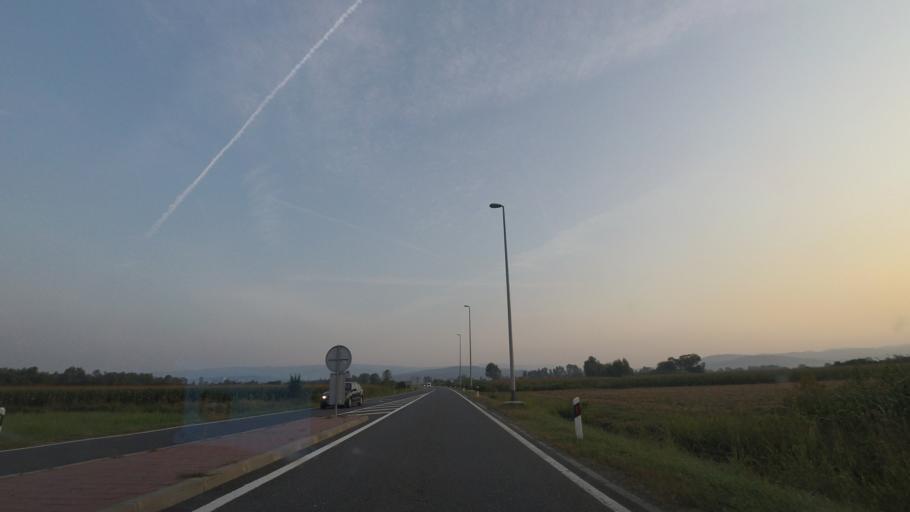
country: HR
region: Brodsko-Posavska
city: Ljupina
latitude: 45.2355
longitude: 17.4112
